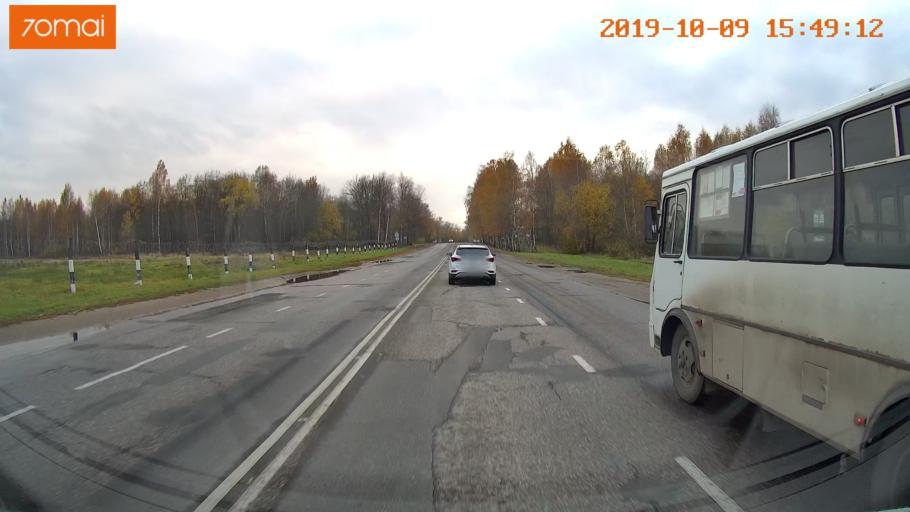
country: RU
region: Kostroma
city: Oktyabr'skiy
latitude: 57.8066
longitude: 41.0075
